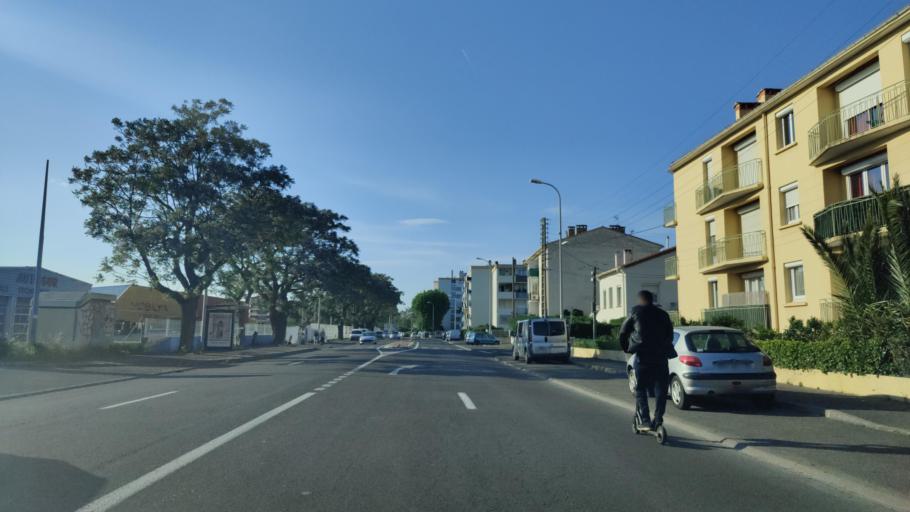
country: FR
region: Languedoc-Roussillon
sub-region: Departement des Pyrenees-Orientales
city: Perpignan
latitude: 42.7083
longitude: 2.8861
